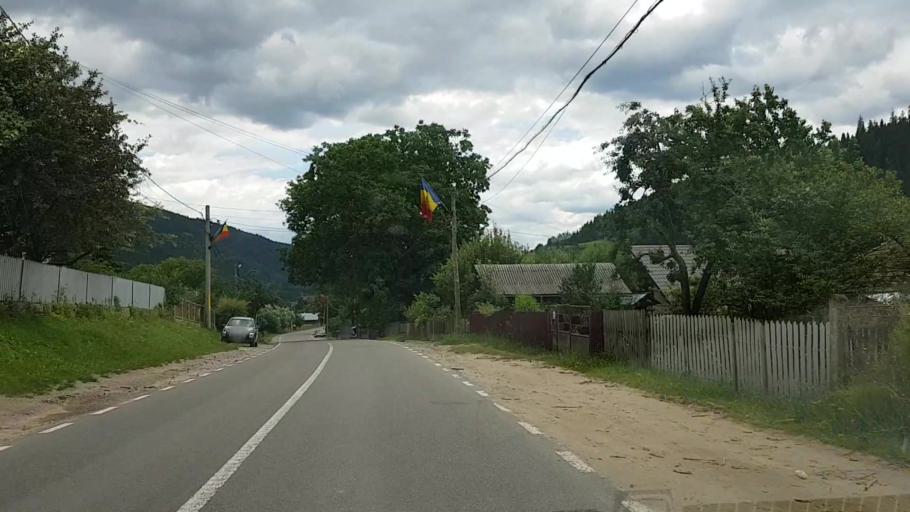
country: RO
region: Neamt
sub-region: Comuna Poiana Teiului
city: Poiana Teiului
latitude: 47.1178
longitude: 25.9180
